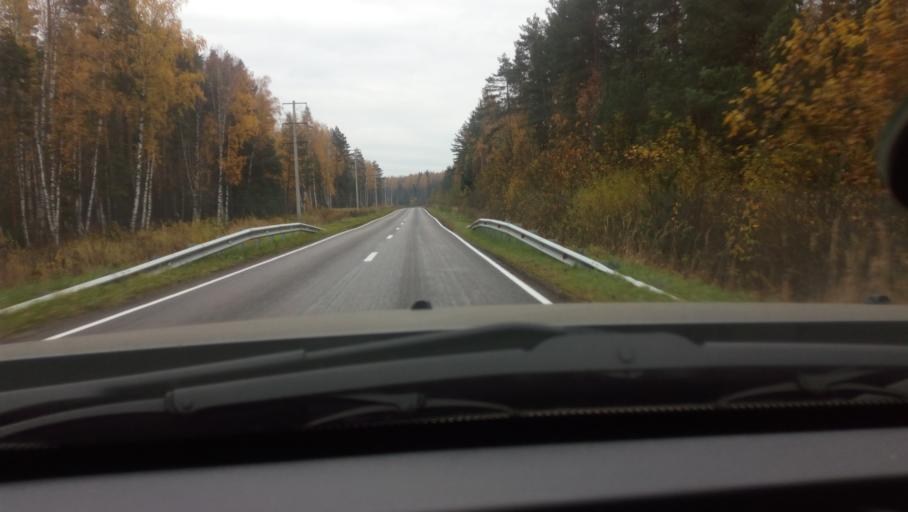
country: RU
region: Moskovskaya
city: Avsyunino
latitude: 55.6018
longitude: 39.2073
